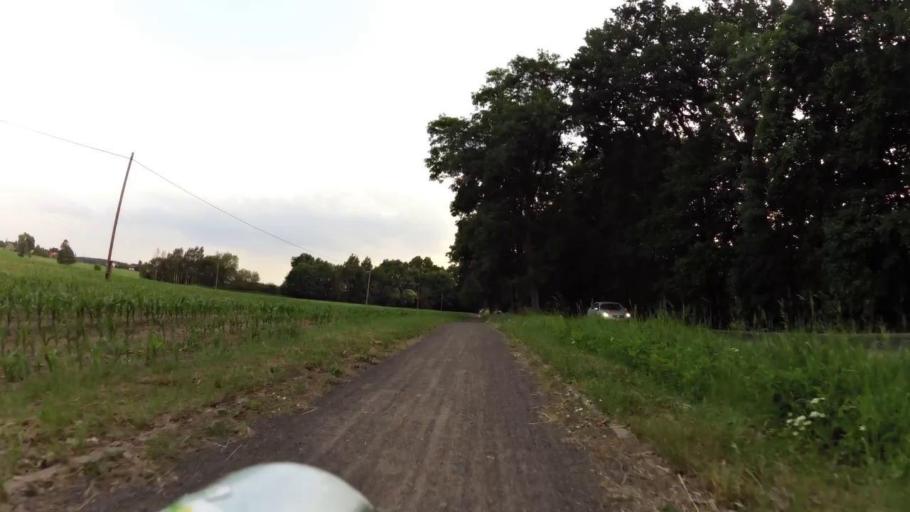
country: PL
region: Kujawsko-Pomorskie
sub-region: Powiat bydgoski
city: Dabrowa Chelminska
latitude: 53.1830
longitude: 18.3343
